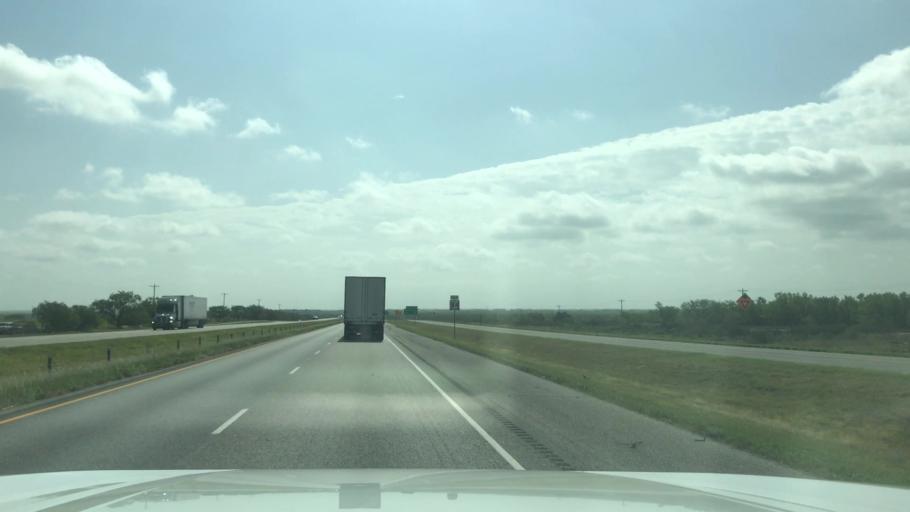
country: US
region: Texas
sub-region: Taylor County
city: Merkel
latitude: 32.4639
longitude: -99.9615
